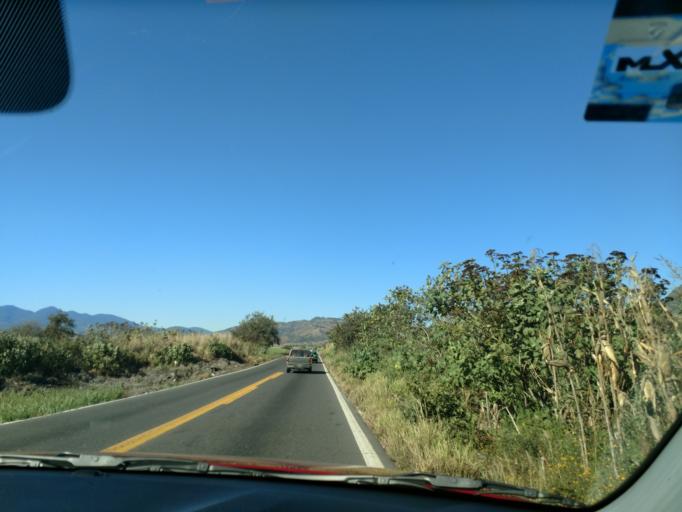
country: MX
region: Nayarit
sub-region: Ahuacatlan
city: Ahuacatlan
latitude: 21.1359
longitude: -104.6068
